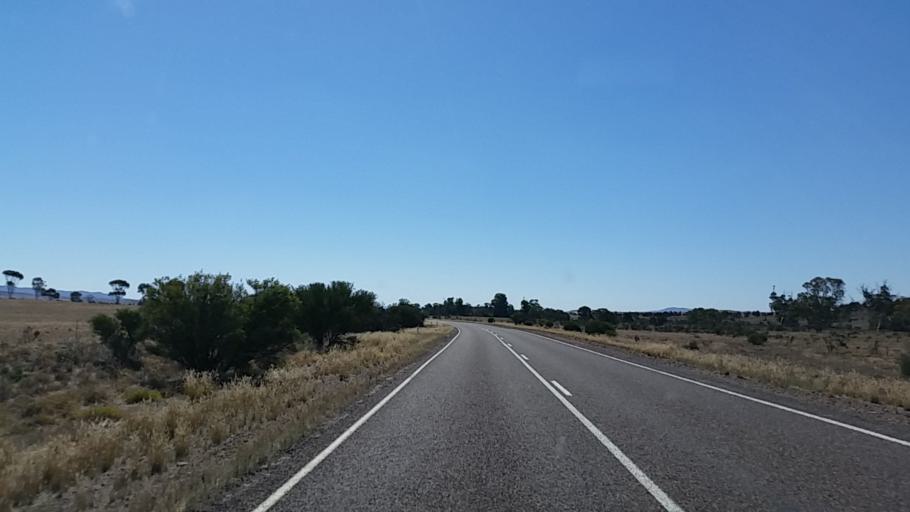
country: AU
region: South Australia
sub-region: Flinders Ranges
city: Quorn
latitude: -32.4903
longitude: 138.5463
